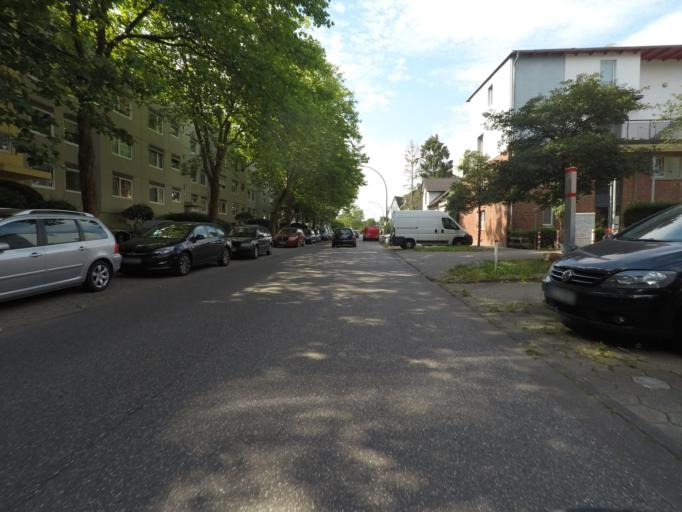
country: DE
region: Hamburg
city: Steilshoop
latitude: 53.6149
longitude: 10.0828
